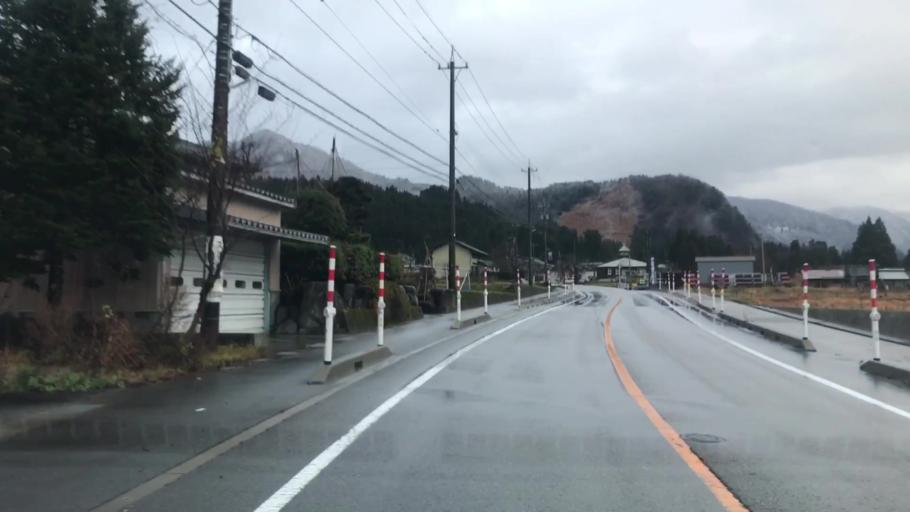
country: JP
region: Toyama
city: Kamiichi
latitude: 36.5793
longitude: 137.3863
